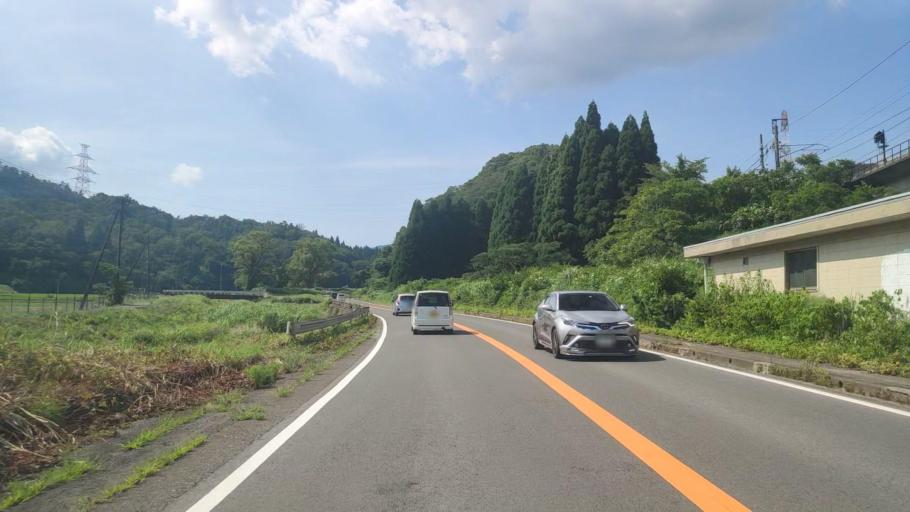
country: JP
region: Fukui
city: Tsuruga
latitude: 35.5450
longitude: 136.1493
